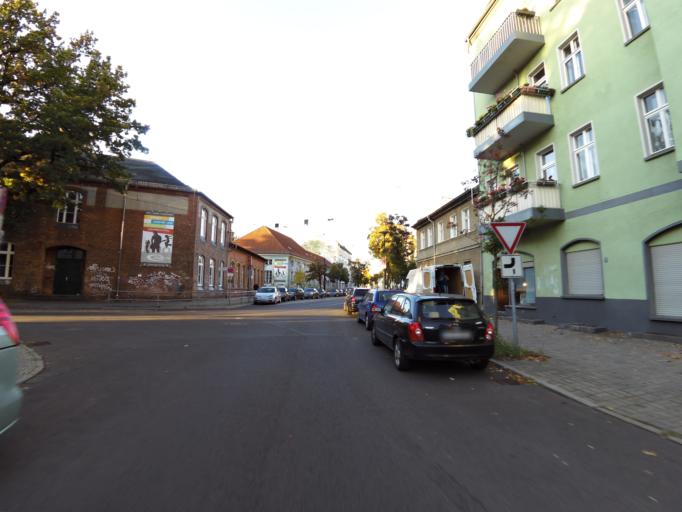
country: DE
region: Berlin
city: Johannisthal
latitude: 52.4402
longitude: 13.5055
